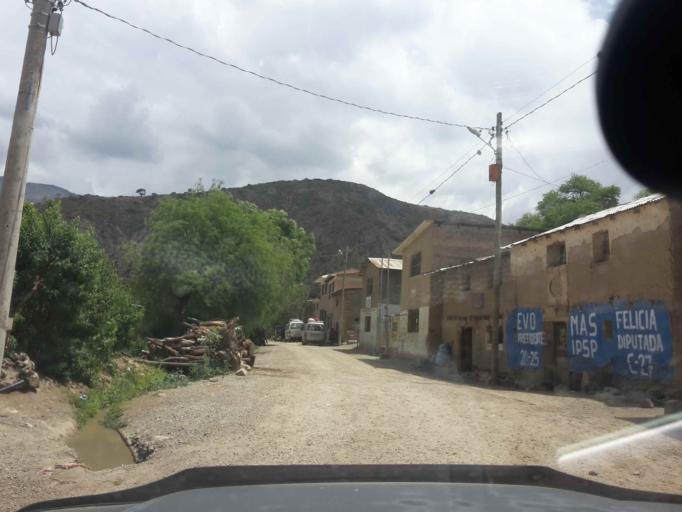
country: BO
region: Cochabamba
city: Sipe Sipe
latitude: -17.5516
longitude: -66.4717
